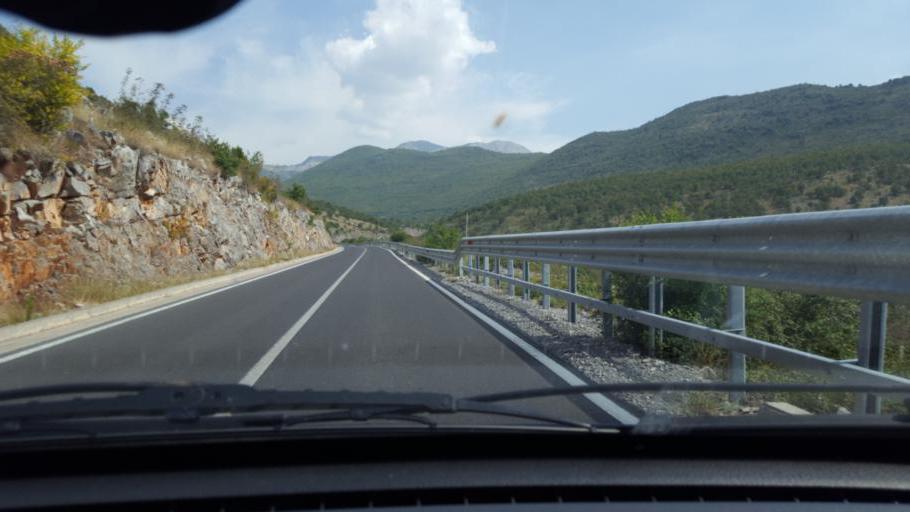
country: AL
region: Shkoder
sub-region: Rrethi i Malesia e Madhe
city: Hot
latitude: 42.3741
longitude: 19.4606
